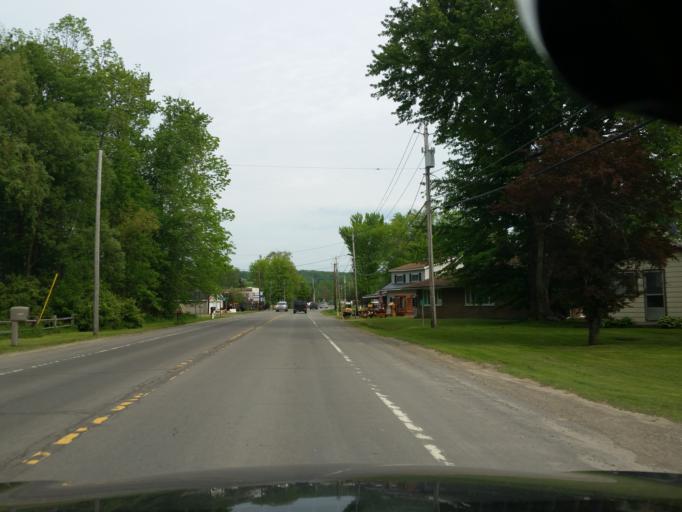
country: US
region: New York
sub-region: Chautauqua County
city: Lakewood
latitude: 42.1031
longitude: -79.3592
